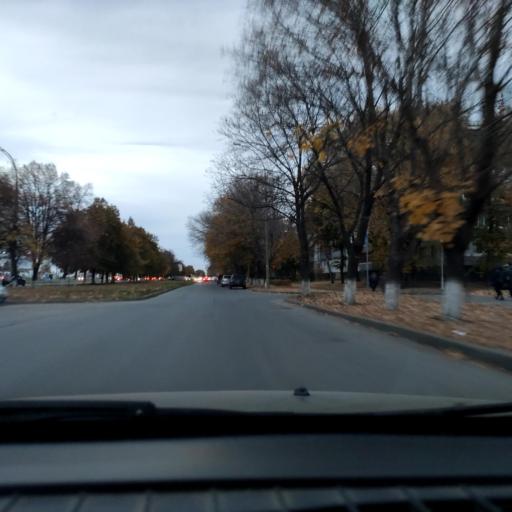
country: RU
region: Samara
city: Tol'yatti
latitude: 53.5342
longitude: 49.2632
